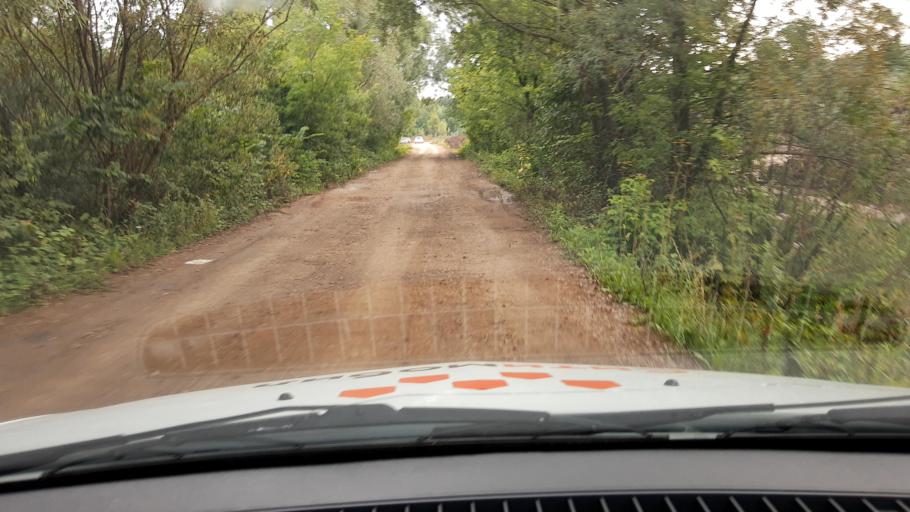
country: RU
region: Bashkortostan
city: Kabakovo
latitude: 54.7000
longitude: 56.1346
